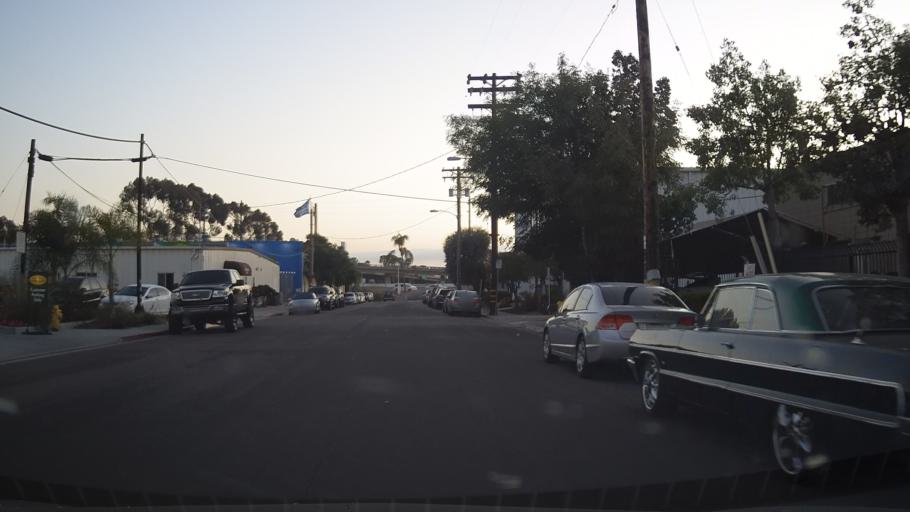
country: US
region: California
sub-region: San Diego County
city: San Diego
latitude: 32.7728
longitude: -117.2042
